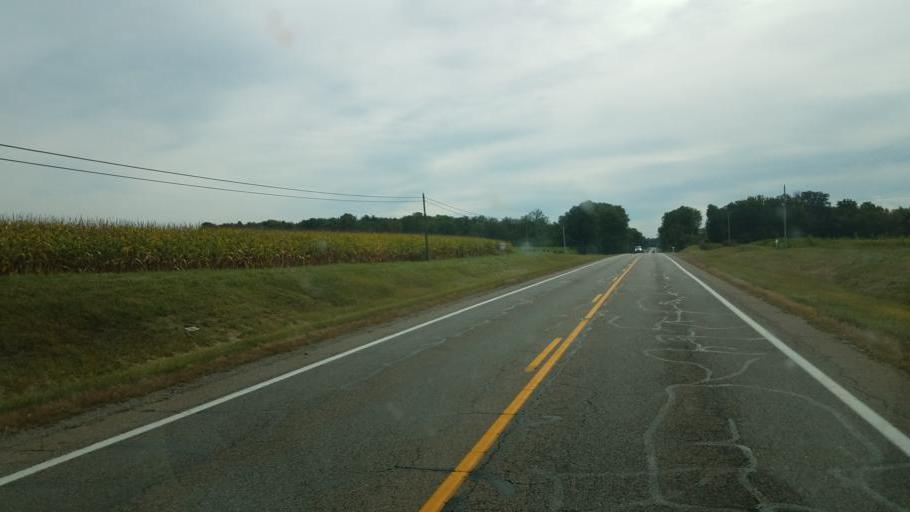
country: US
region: Ohio
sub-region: Morrow County
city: Mount Gilead
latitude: 40.4892
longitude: -82.7031
